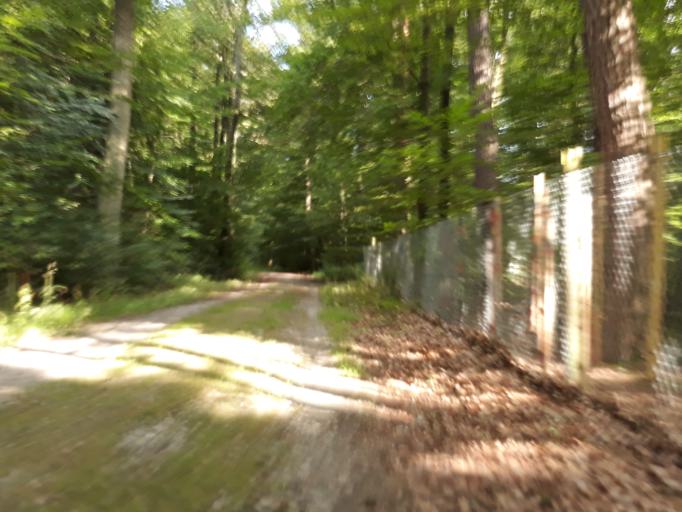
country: DE
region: Baden-Wuerttemberg
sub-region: Regierungsbezirk Stuttgart
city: Schonaich
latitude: 48.6736
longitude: 9.0401
